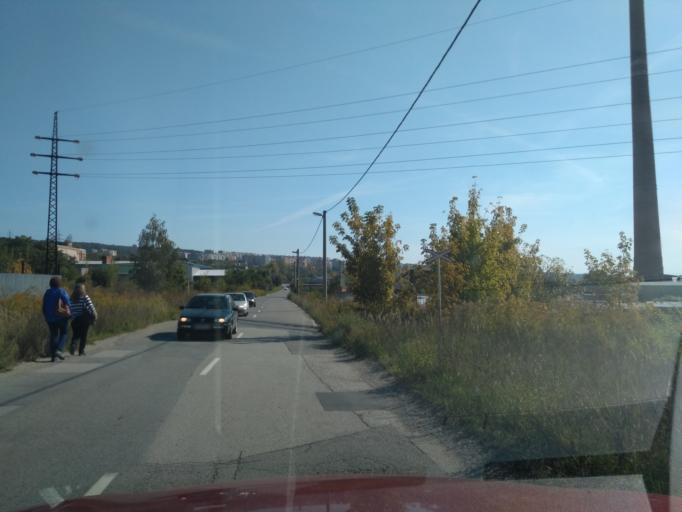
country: SK
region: Kosicky
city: Kosice
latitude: 48.7517
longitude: 21.2608
